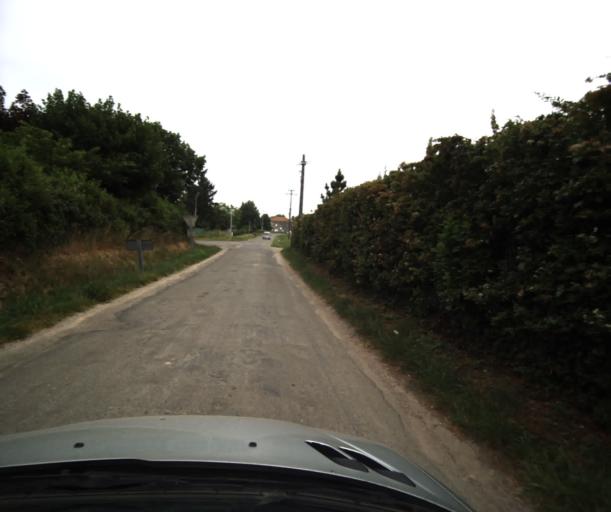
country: FR
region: Midi-Pyrenees
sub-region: Departement du Tarn-et-Garonne
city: Saint-Nicolas-de-la-Grave
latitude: 44.0496
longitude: 1.0166
